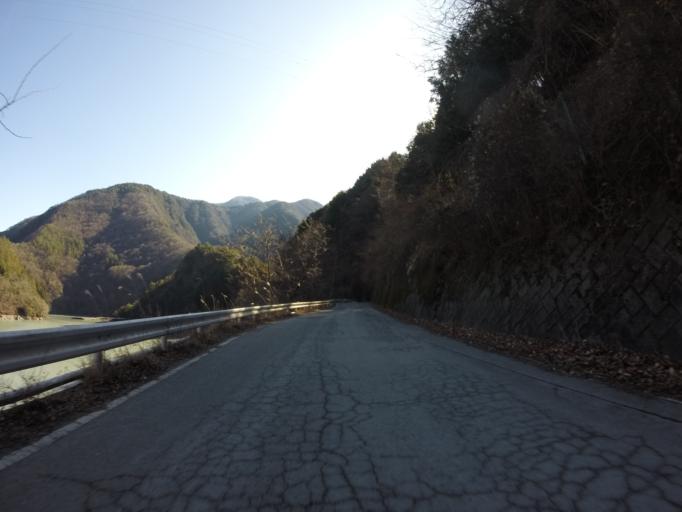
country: JP
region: Yamanashi
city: Ryuo
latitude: 35.4080
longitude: 138.3281
